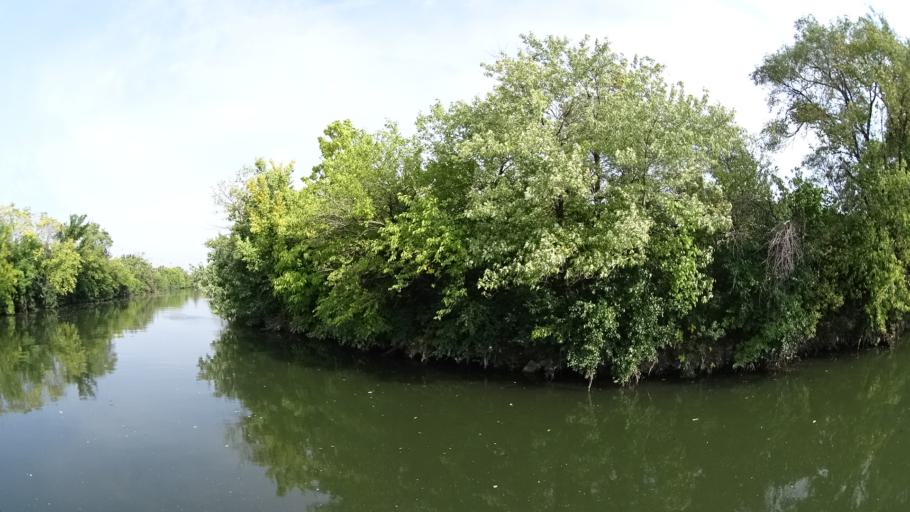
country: US
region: Illinois
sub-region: Cook County
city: Chicago
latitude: 41.8348
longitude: -87.6610
